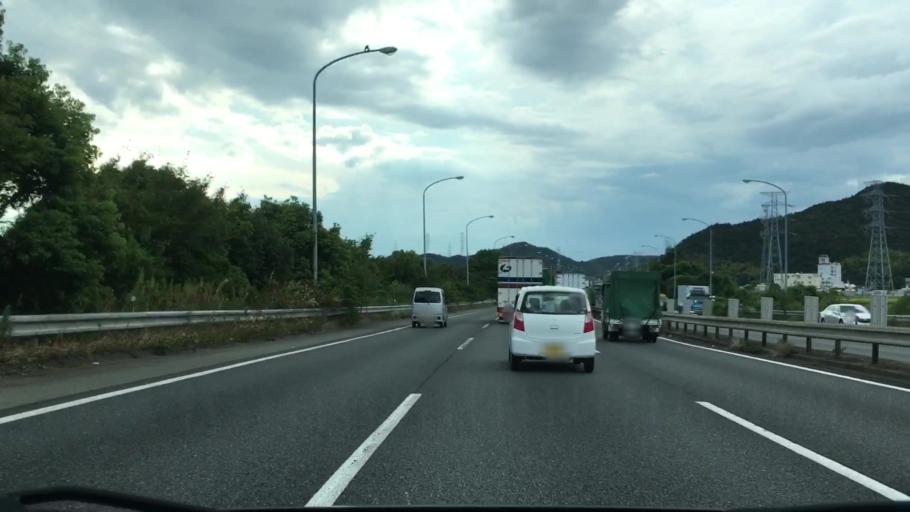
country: JP
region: Hyogo
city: Shirahamacho-usazakiminami
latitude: 34.7984
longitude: 134.7350
